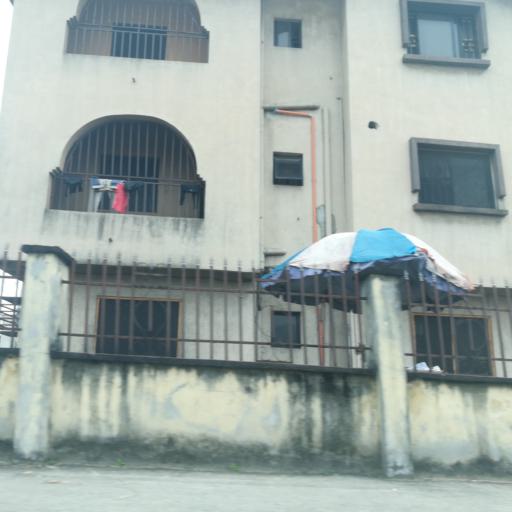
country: NG
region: Rivers
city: Port Harcourt
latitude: 4.8010
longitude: 7.0026
